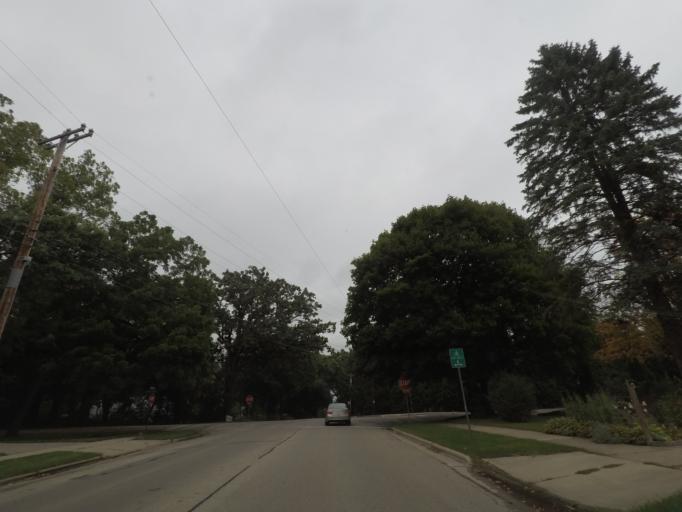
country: US
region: Wisconsin
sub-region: Dane County
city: Shorewood Hills
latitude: 43.0388
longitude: -89.4734
